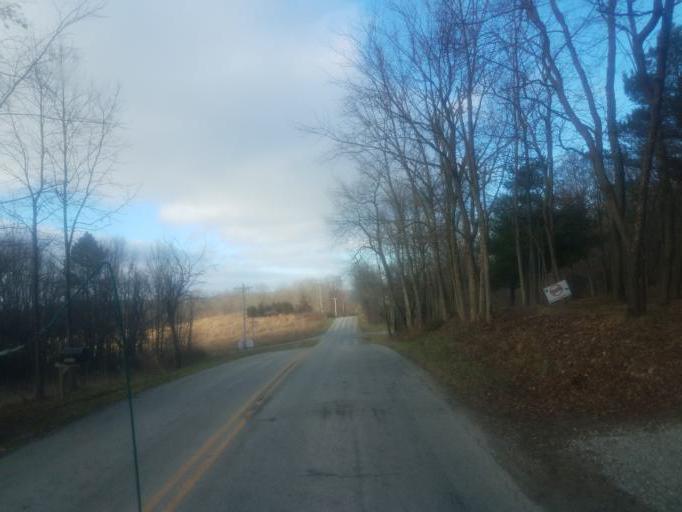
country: US
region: Ohio
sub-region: Sandusky County
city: Bellville
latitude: 40.6047
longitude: -82.3772
